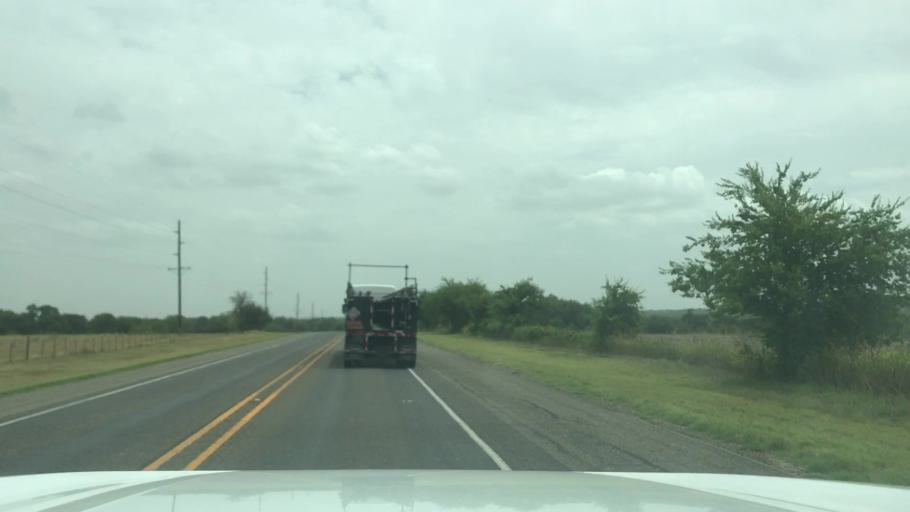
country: US
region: Texas
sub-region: Bosque County
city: Valley Mills
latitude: 31.7009
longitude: -97.5416
